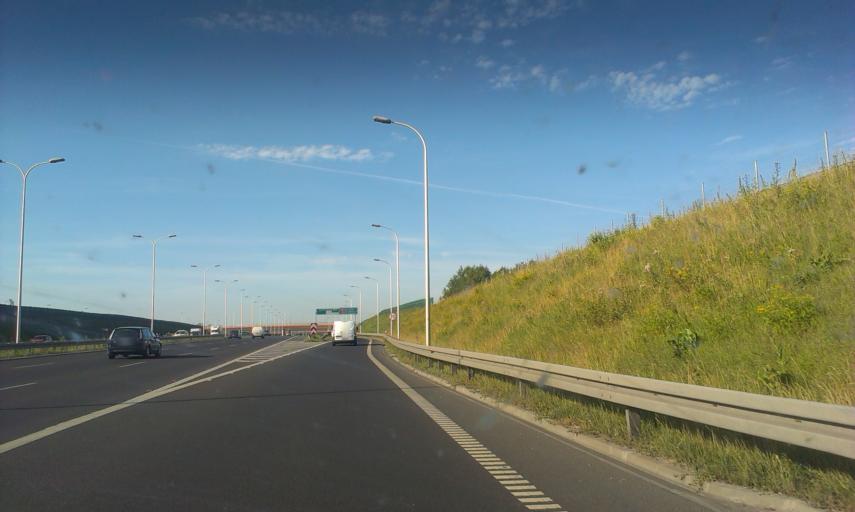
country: PL
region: Masovian Voivodeship
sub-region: Powiat pruszkowski
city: Nowe Grocholice
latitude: 52.1801
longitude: 20.9147
